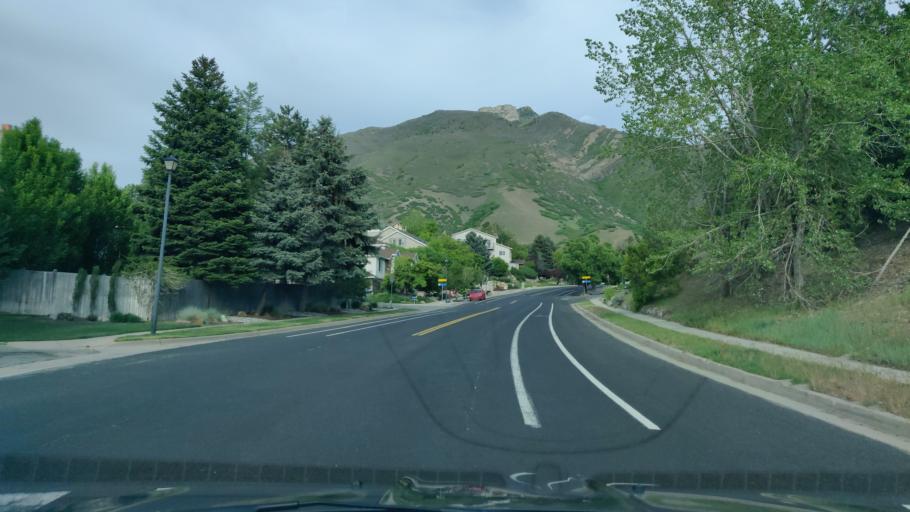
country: US
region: Utah
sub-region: Salt Lake County
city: Cottonwood Heights
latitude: 40.6050
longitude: -111.8027
